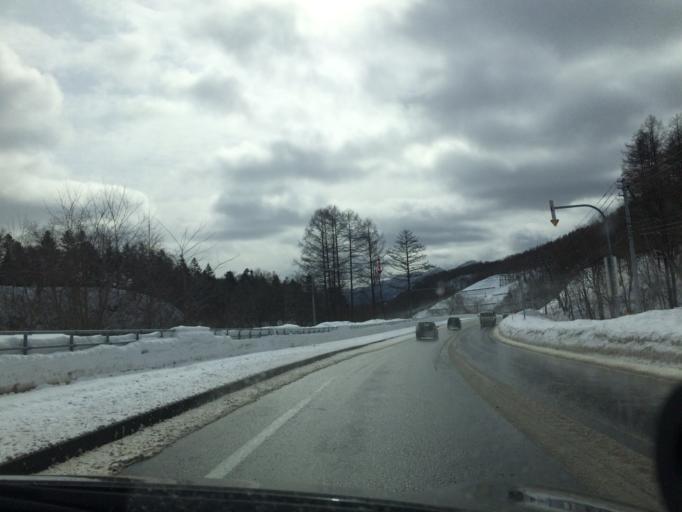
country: JP
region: Hokkaido
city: Iwamizawa
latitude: 43.0129
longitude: 142.0036
